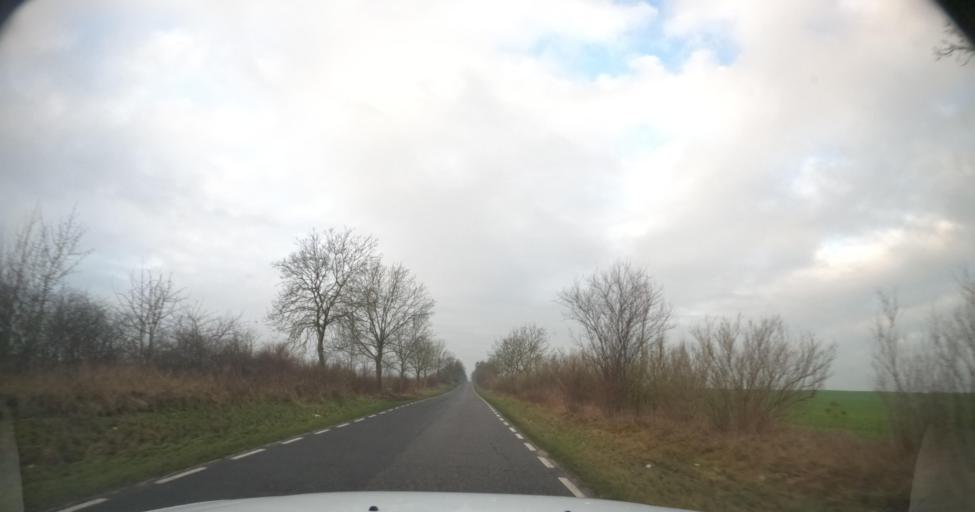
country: PL
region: West Pomeranian Voivodeship
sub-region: Powiat mysliborski
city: Debno
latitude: 52.7359
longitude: 14.6368
